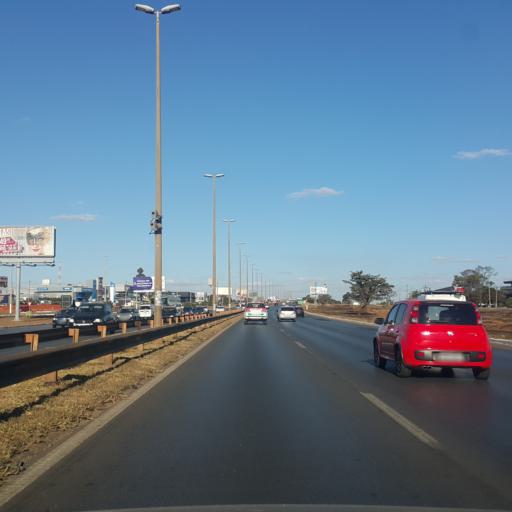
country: BR
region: Federal District
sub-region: Brasilia
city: Brasilia
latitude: -15.7905
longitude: -47.9803
